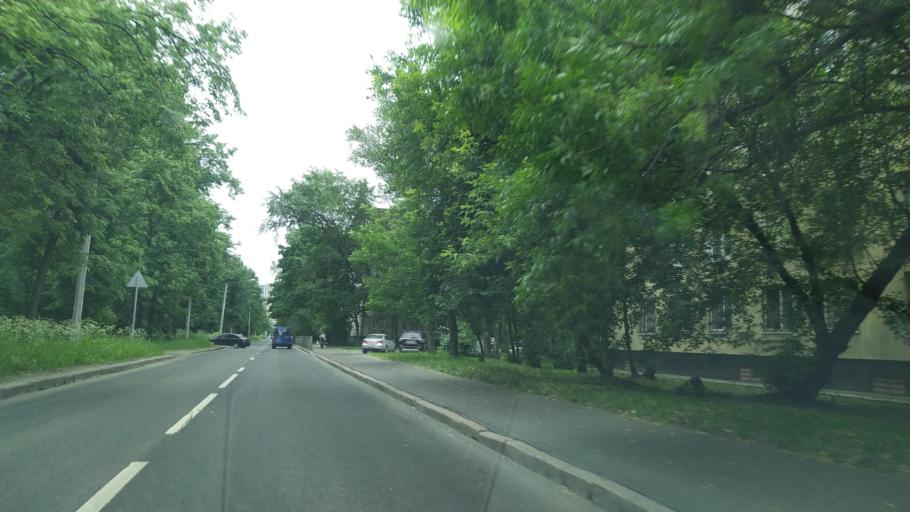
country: RU
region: St.-Petersburg
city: Avtovo
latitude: 59.8474
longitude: 30.2998
